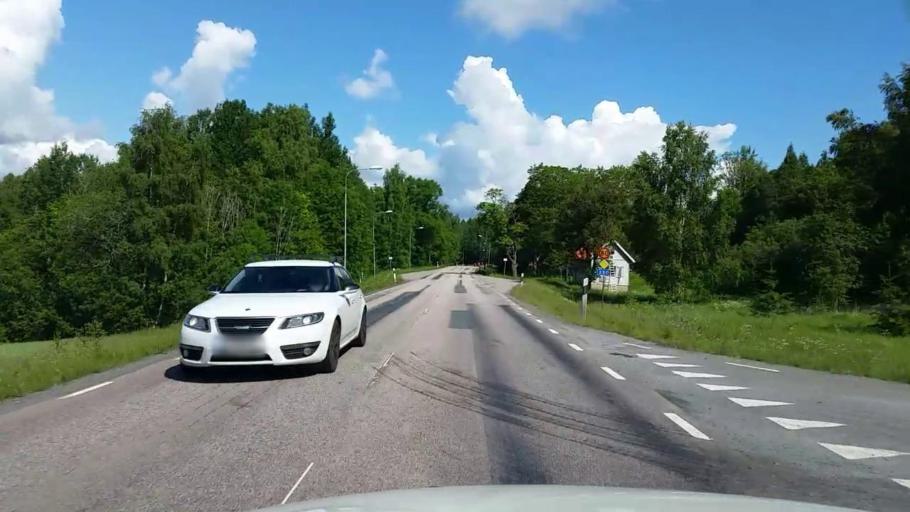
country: SE
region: Vaestmanland
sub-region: Kopings Kommun
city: Kolsva
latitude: 59.6230
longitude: 15.8197
